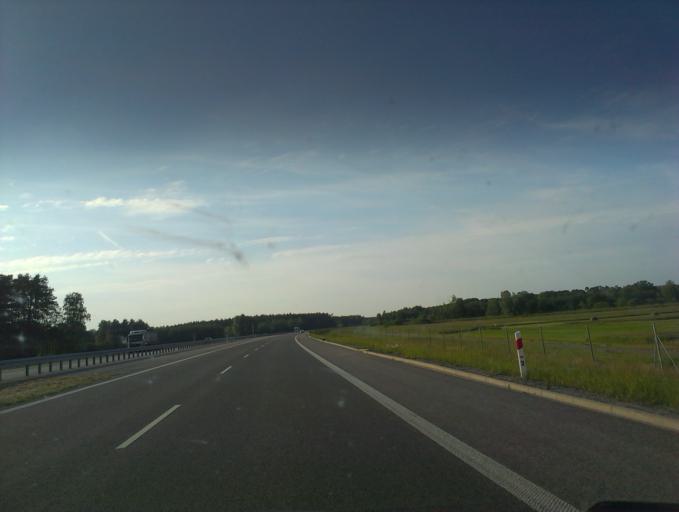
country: PL
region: Greater Poland Voivodeship
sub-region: Powiat rawicki
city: Rawicz
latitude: 51.6155
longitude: 16.7981
